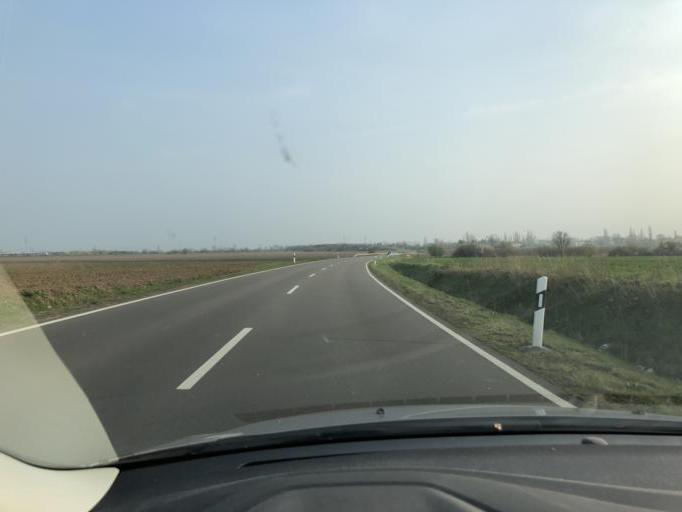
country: DE
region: Saxony-Anhalt
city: Brehna
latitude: 51.5638
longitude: 12.2263
